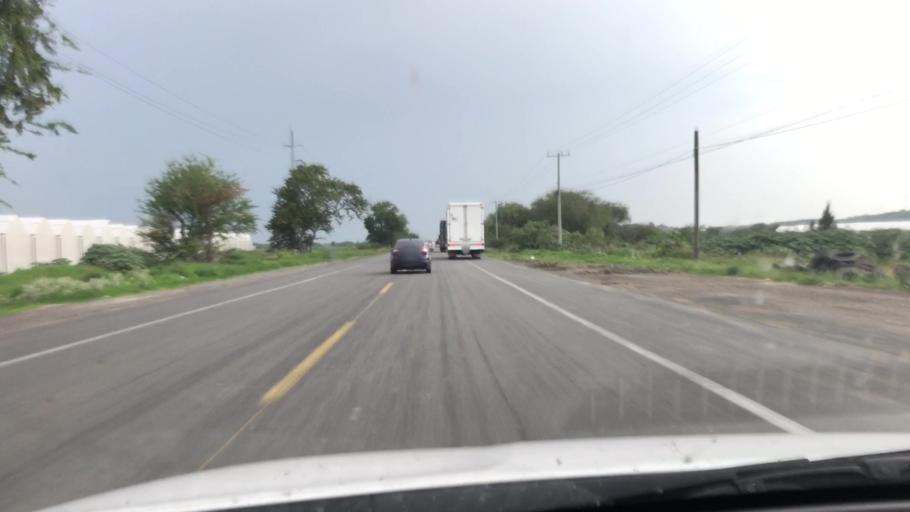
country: MX
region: Michoacan
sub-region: Vista Hermosa
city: Los Pilares
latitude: 20.2756
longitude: -102.3954
